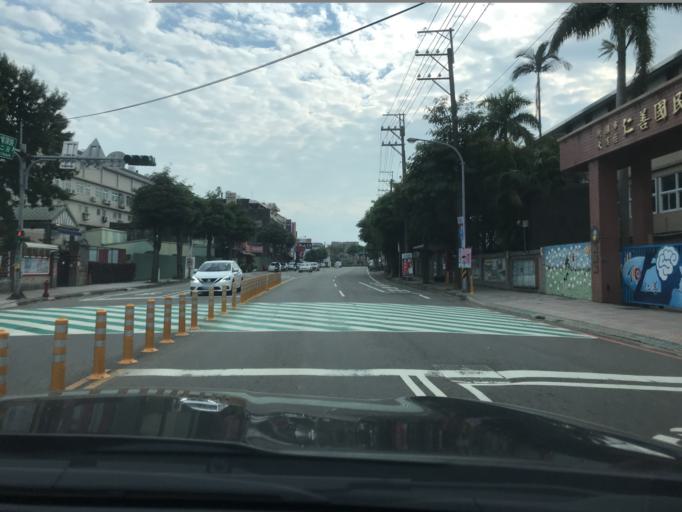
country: TW
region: Taiwan
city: Daxi
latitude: 24.9094
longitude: 121.2793
